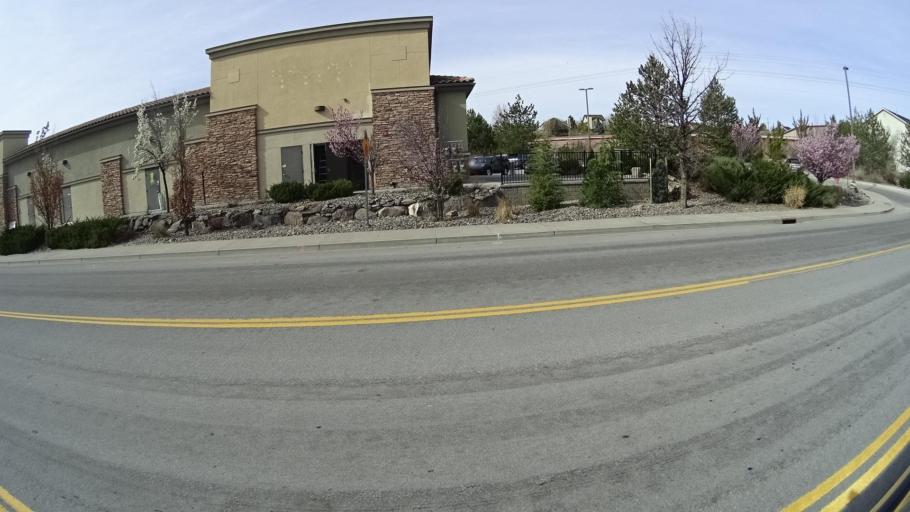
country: US
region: Nevada
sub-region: Washoe County
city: Reno
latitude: 39.5406
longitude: -119.8629
